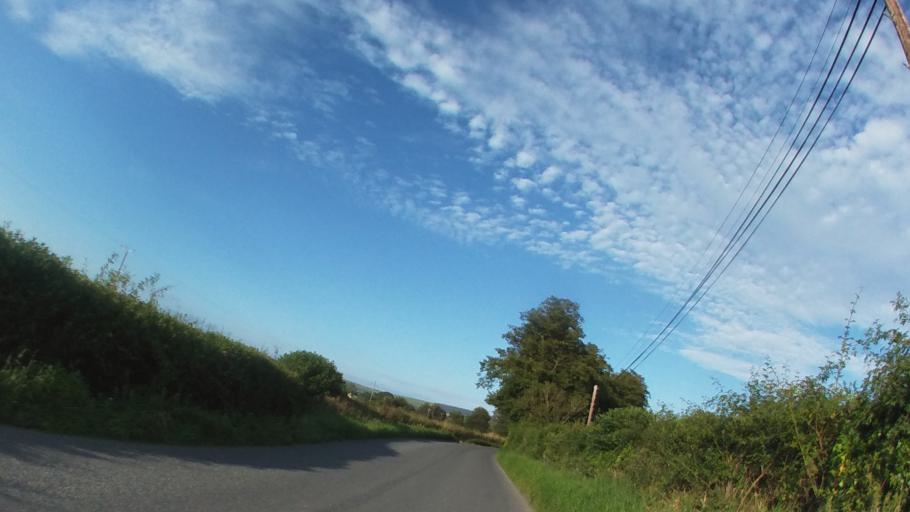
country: IE
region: Leinster
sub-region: Kilkenny
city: Kilkenny
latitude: 52.6755
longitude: -7.1963
